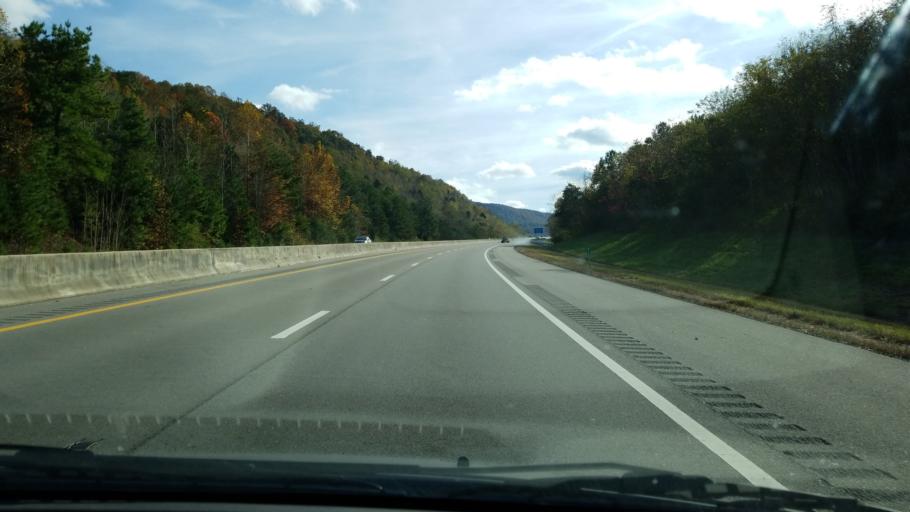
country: US
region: Tennessee
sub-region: Sequatchie County
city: Dunlap
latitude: 35.3823
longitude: -85.3305
